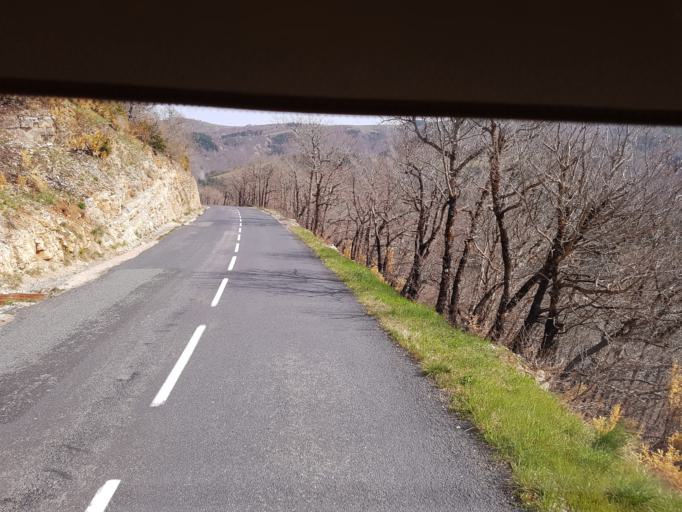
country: FR
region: Languedoc-Roussillon
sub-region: Departement de la Lozere
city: Meyrueis
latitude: 44.2098
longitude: 3.5254
